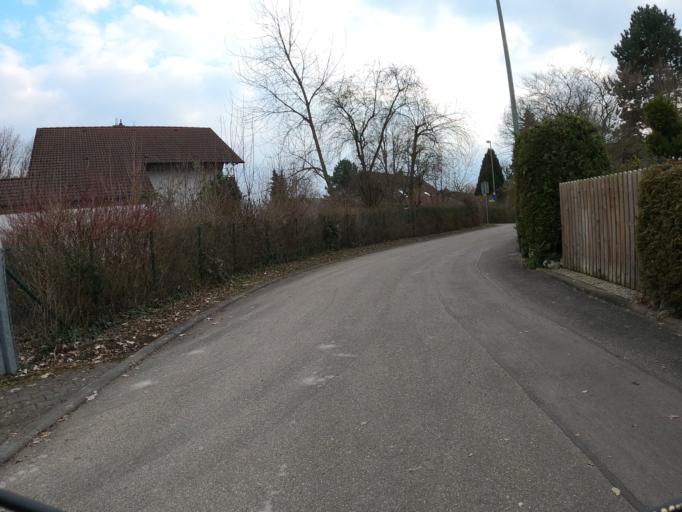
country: DE
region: Bavaria
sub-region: Swabia
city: Nersingen
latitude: 48.4354
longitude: 10.1131
